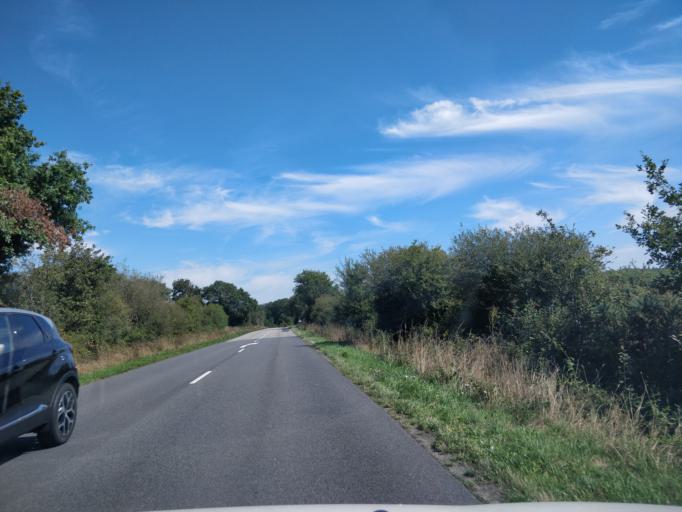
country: FR
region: Pays de la Loire
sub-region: Departement de la Loire-Atlantique
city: Plesse
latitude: 47.5683
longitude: -1.8678
